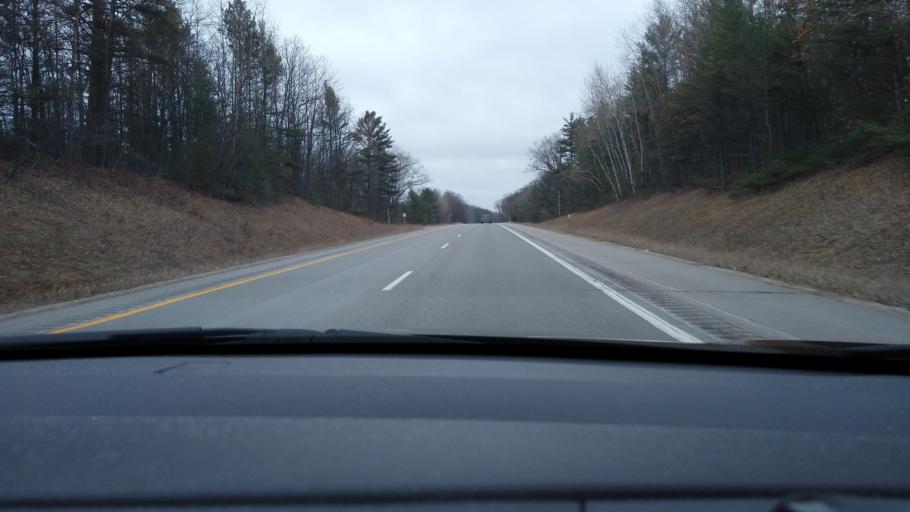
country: US
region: Michigan
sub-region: Otsego County
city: Gaylord
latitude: 44.9184
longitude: -84.6863
